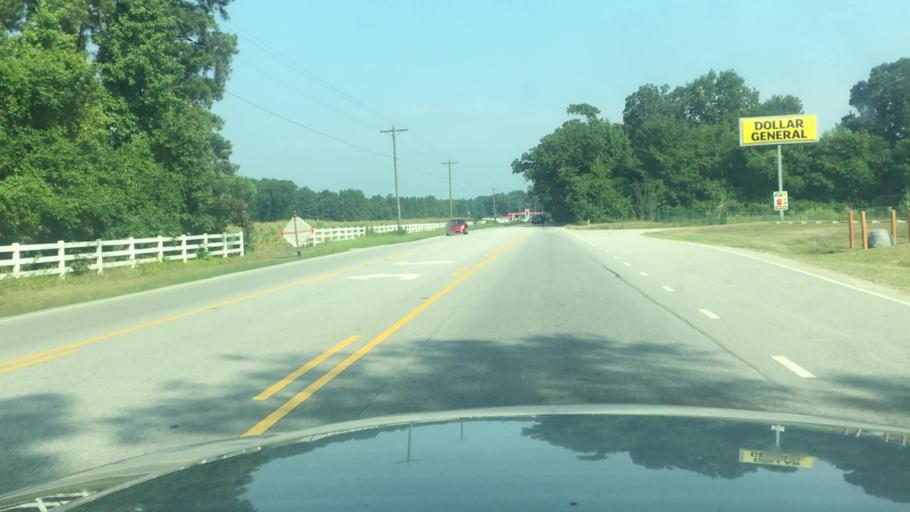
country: US
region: North Carolina
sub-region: Cumberland County
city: Hope Mills
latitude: 34.9310
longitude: -78.9159
